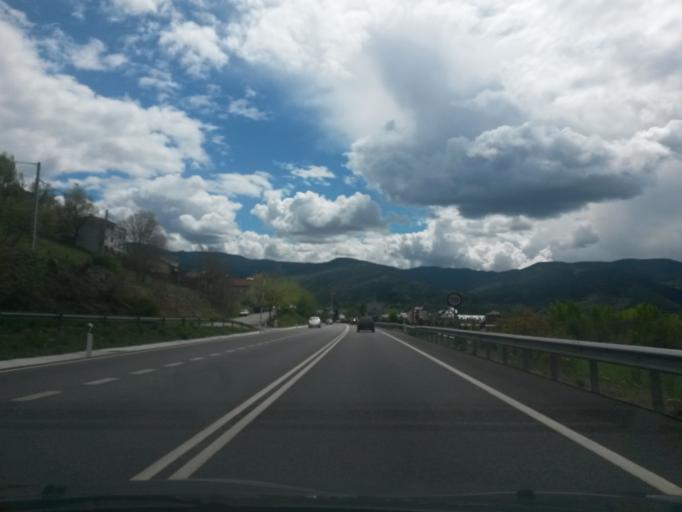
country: ES
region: Catalonia
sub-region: Provincia de Lleida
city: la Seu d'Urgell
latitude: 42.3659
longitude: 1.4550
